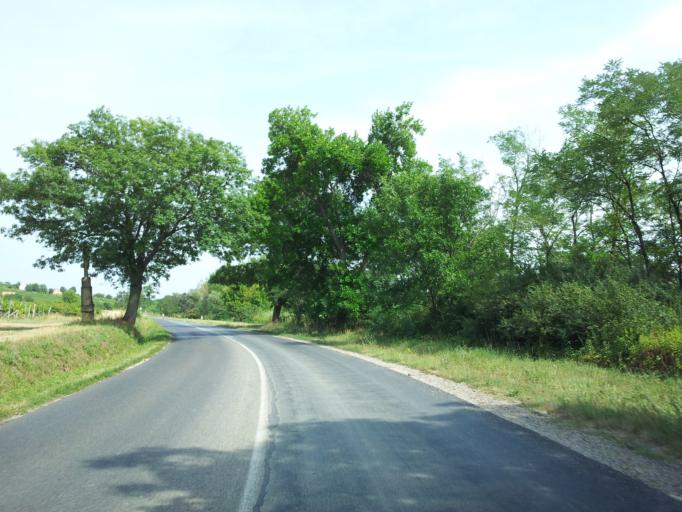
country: HU
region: Veszprem
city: Badacsonytomaj
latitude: 46.8542
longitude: 17.5345
